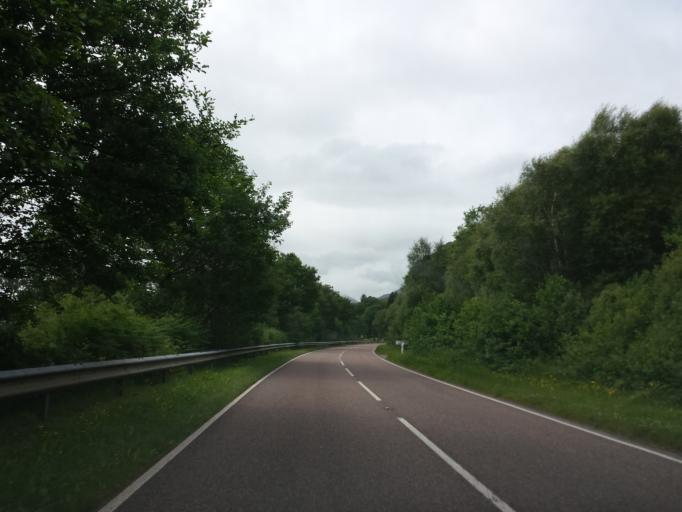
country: GB
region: Scotland
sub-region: Highland
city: Fort William
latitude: 56.8579
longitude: -5.3136
